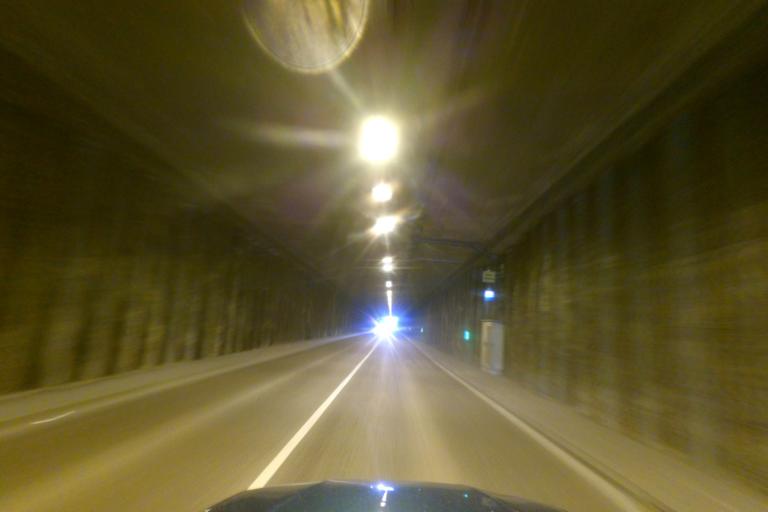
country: DE
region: Baden-Wuerttemberg
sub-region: Regierungsbezirk Stuttgart
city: Huttlingen
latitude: 48.8684
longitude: 10.1088
